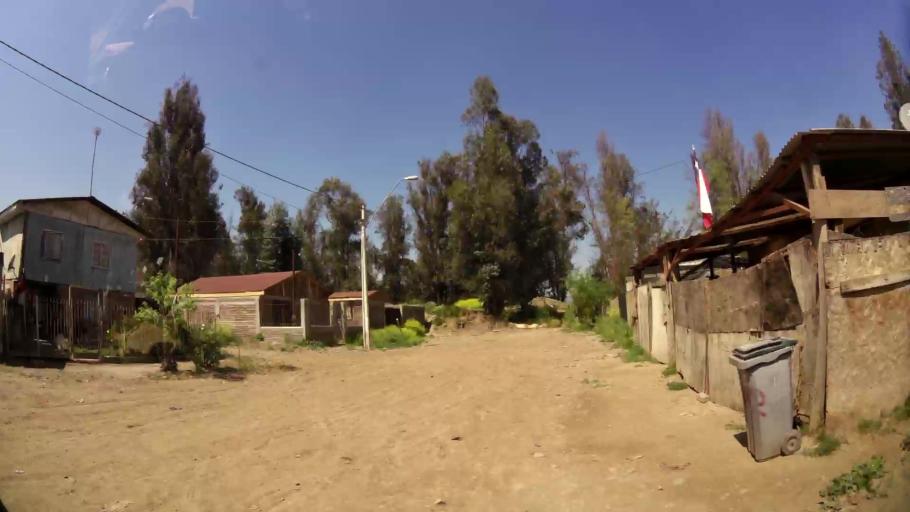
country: CL
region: Santiago Metropolitan
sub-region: Provincia de Talagante
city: Penaflor
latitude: -33.5872
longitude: -70.8137
